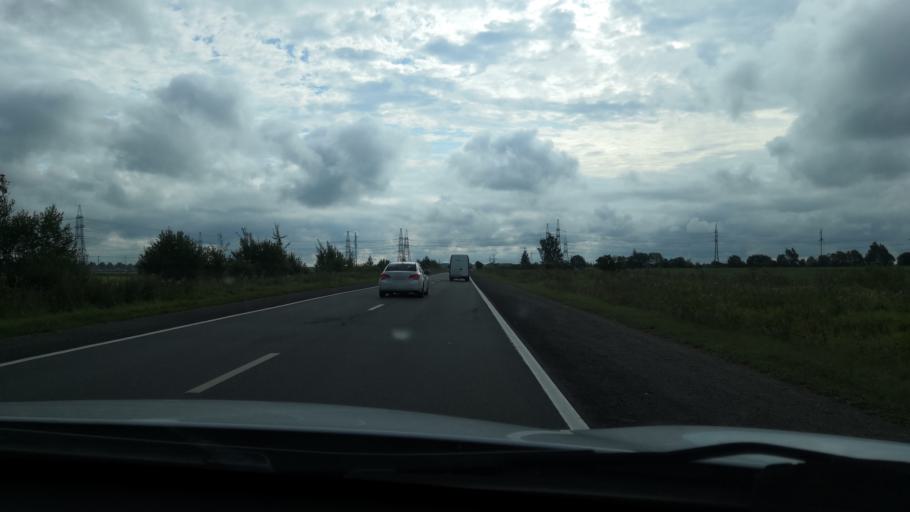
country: RU
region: Leningrad
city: Fedorovskoye
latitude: 59.7077
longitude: 30.5246
